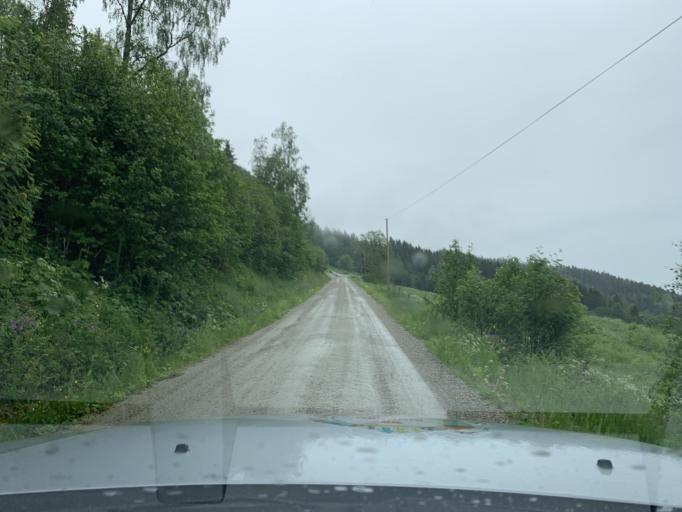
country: NO
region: Oppland
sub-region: Oyer
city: Tretten
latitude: 61.3883
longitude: 10.2803
